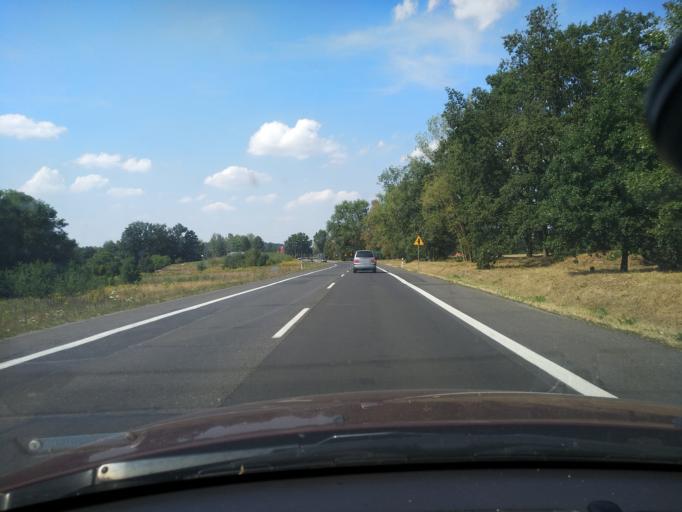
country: PL
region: Lower Silesian Voivodeship
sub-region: Powiat lubanski
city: Luban
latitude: 51.0976
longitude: 15.3127
